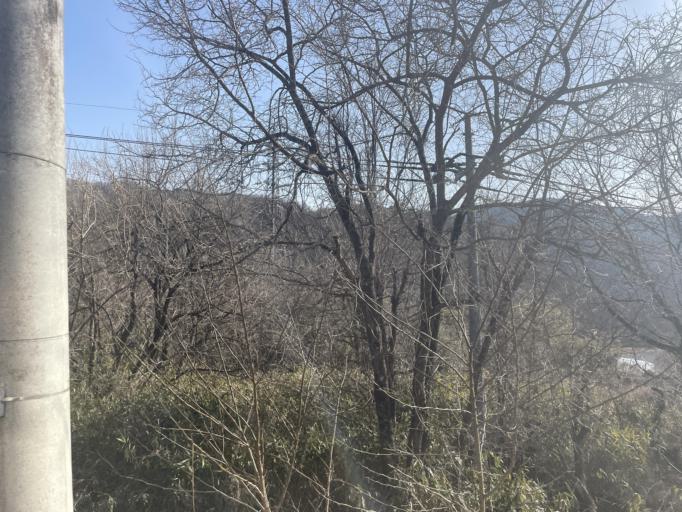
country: JP
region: Gunma
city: Nakanojomachi
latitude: 36.5520
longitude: 138.6117
